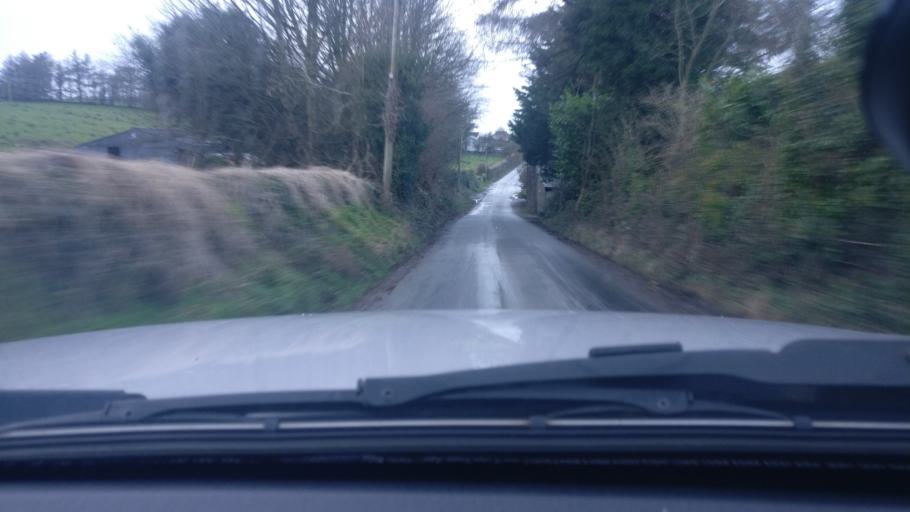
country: IE
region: Connaught
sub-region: County Galway
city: Loughrea
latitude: 53.1634
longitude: -8.5513
